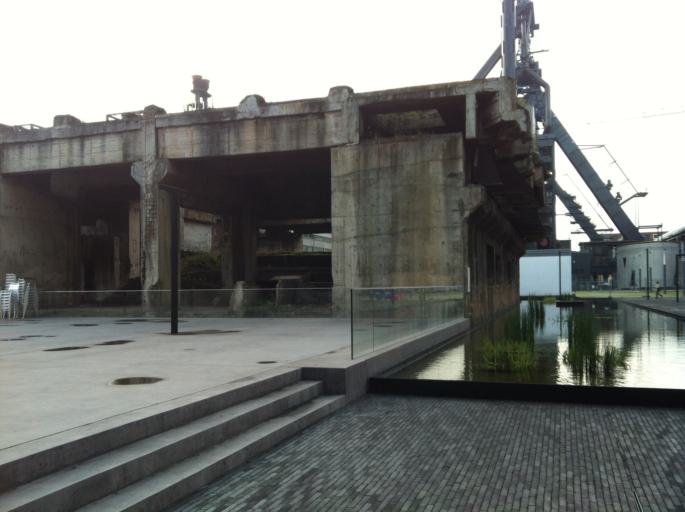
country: FR
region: Lorraine
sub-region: Departement de la Moselle
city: Russange
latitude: 49.5038
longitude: 5.9491
